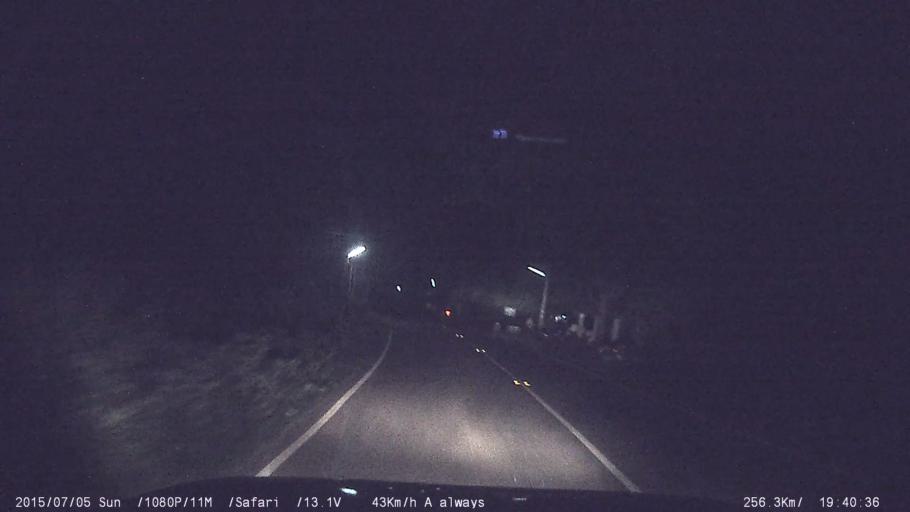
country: IN
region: Kerala
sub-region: Palakkad district
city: Palakkad
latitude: 10.7530
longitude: 76.5596
